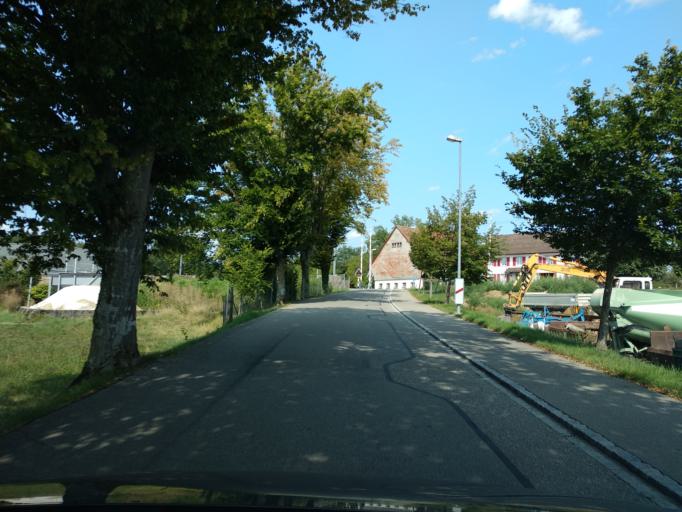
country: CH
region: Zurich
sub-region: Bezirk Andelfingen
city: Marthalen
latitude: 47.6353
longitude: 8.6514
